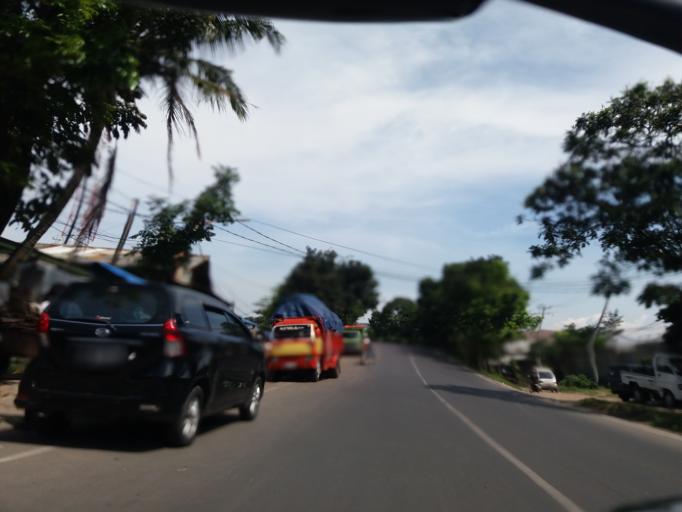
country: ID
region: West Java
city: Margahayukencana
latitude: -6.9301
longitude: 107.5731
